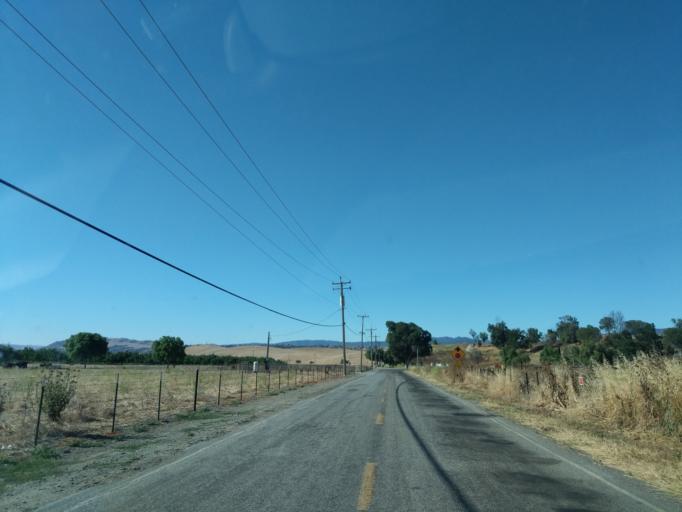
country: US
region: California
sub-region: San Benito County
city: Ridgemark
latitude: 36.8116
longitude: -121.3454
